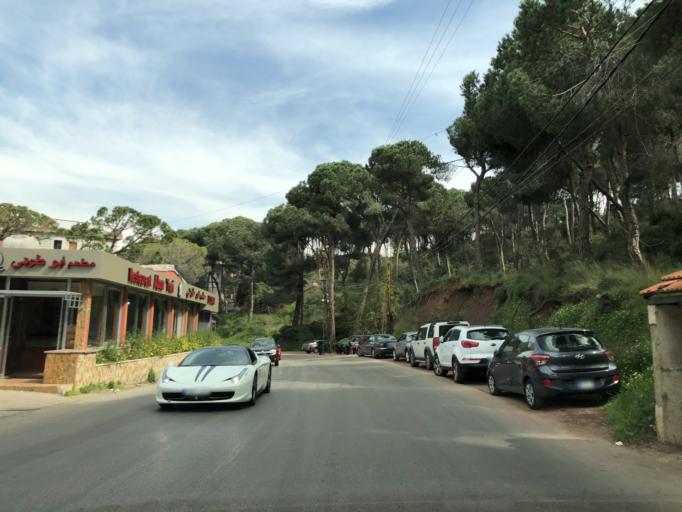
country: LB
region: Mont-Liban
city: Bhamdoun el Mhatta
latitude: 33.8890
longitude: 35.6625
